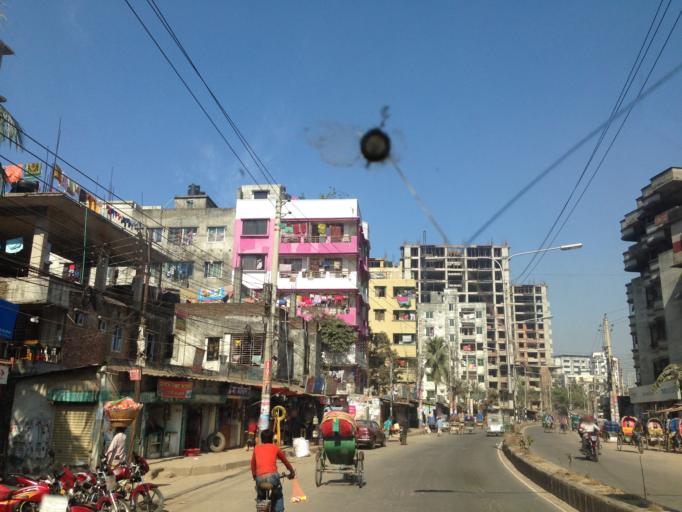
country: BD
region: Dhaka
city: Azimpur
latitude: 23.8114
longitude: 90.3608
